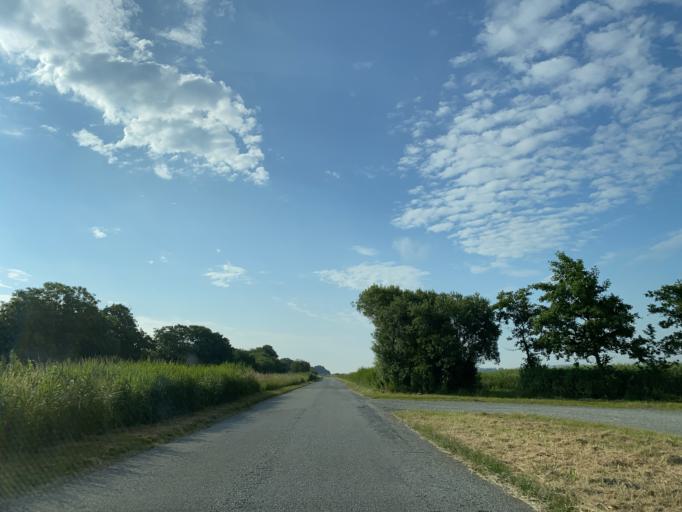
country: DK
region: South Denmark
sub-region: Haderslev Kommune
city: Haderslev
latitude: 55.1735
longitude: 9.4829
